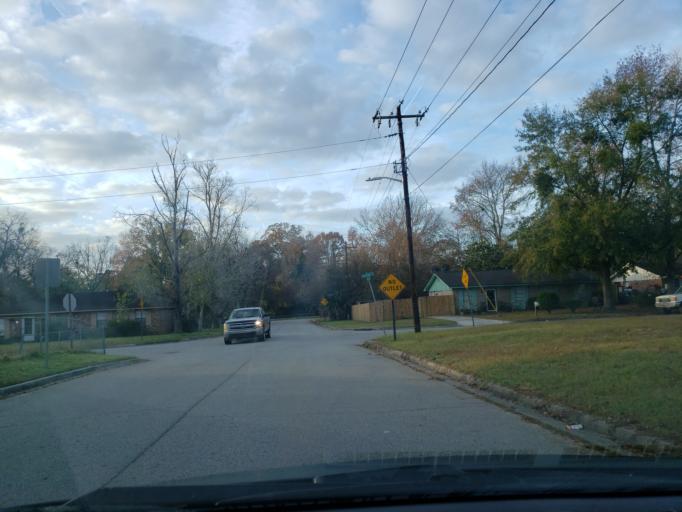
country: US
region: Georgia
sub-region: Chatham County
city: Montgomery
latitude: 31.9956
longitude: -81.1220
